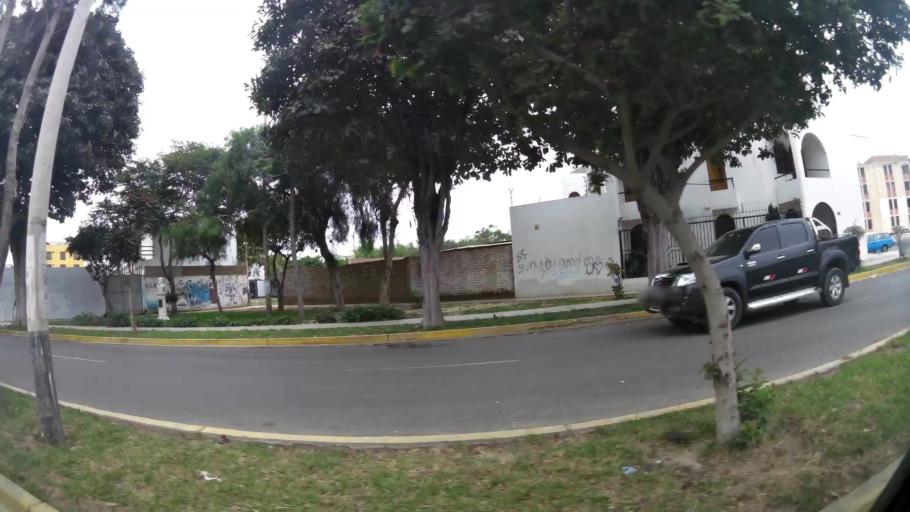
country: PE
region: La Libertad
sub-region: Provincia de Trujillo
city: Buenos Aires
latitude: -8.1249
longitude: -79.0414
